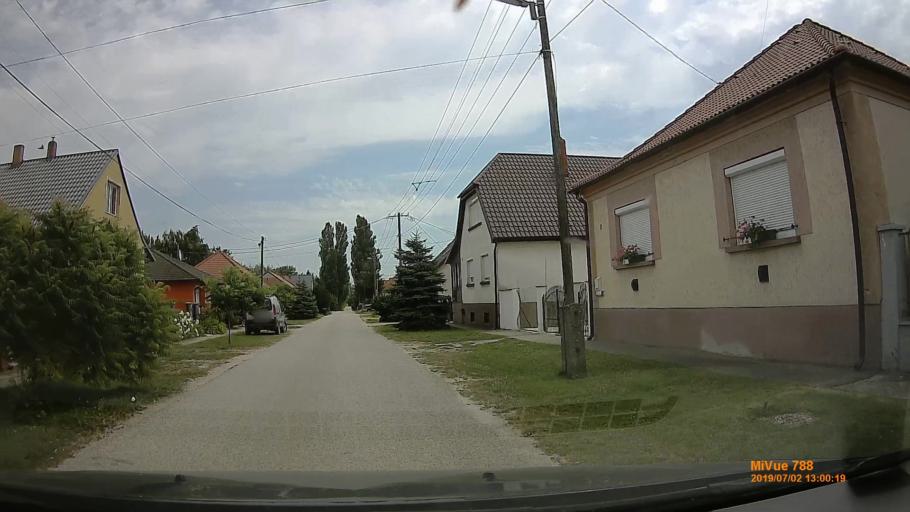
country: HU
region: Gyor-Moson-Sopron
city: Halaszi
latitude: 47.8578
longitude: 17.3261
